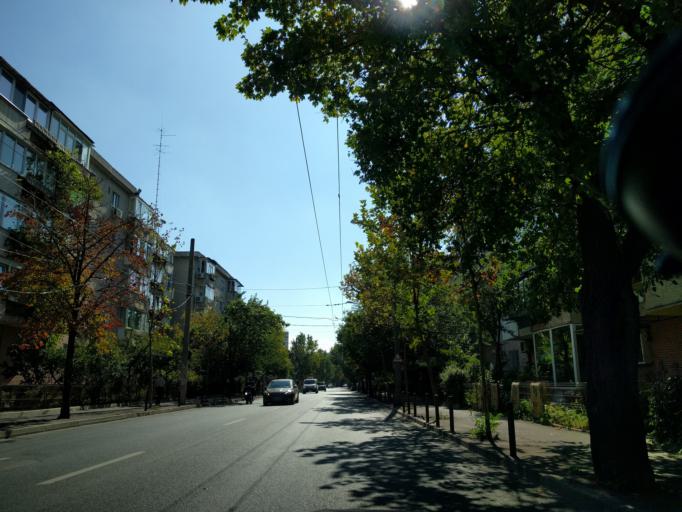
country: RO
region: Bucuresti
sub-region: Municipiul Bucuresti
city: Bucharest
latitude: 44.4277
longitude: 26.1335
